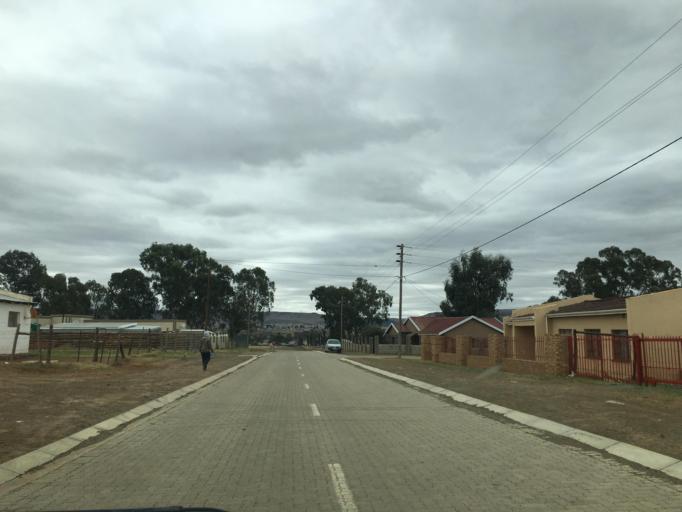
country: ZA
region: Eastern Cape
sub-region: Chris Hani District Municipality
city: Cala
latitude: -31.5346
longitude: 27.6906
